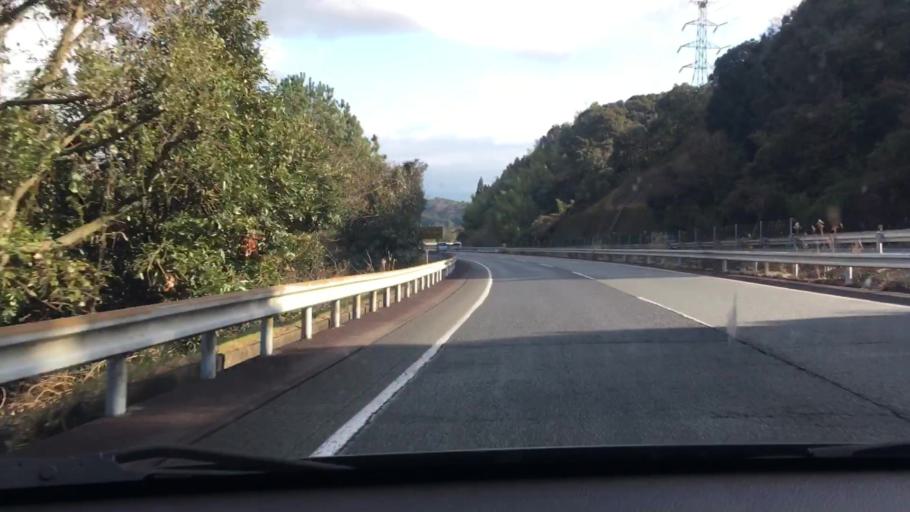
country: JP
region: Kumamoto
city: Hitoyoshi
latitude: 32.2678
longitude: 130.7621
